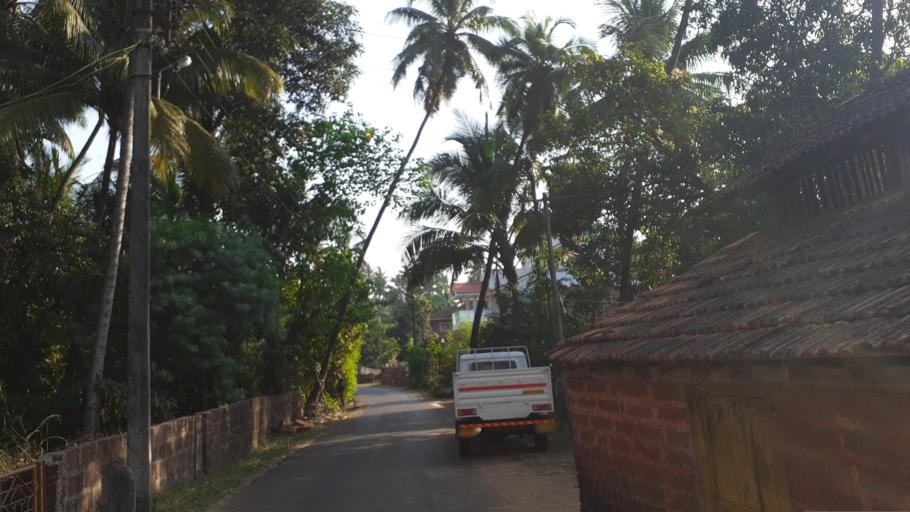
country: IN
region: Maharashtra
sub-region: Ratnagiri
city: Ratnagiri
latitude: 17.2157
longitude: 73.2479
